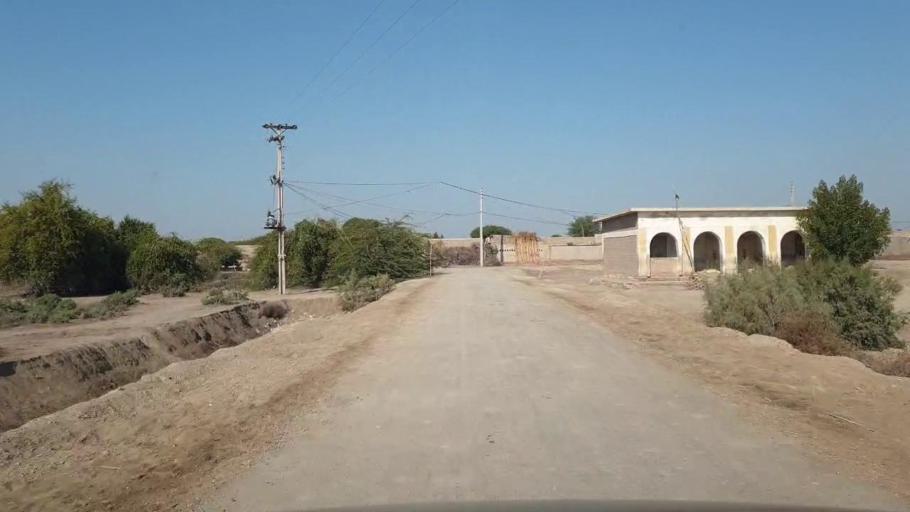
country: PK
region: Sindh
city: Shahpur Chakar
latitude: 26.1575
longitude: 68.6766
